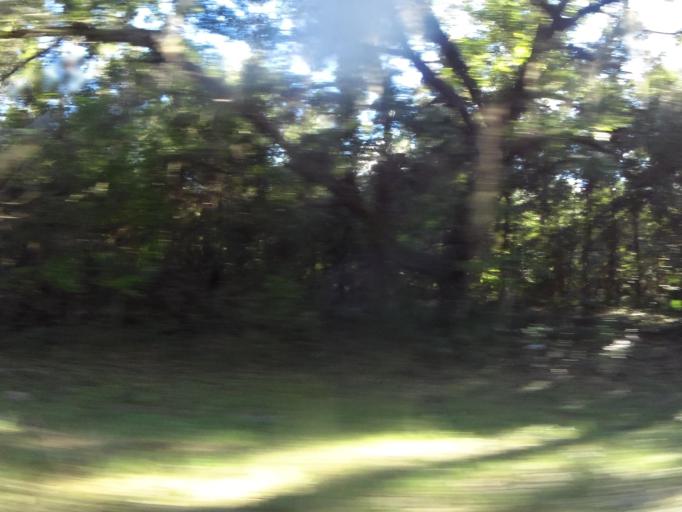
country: US
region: Florida
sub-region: Alachua County
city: Hawthorne
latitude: 29.5278
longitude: -82.1954
